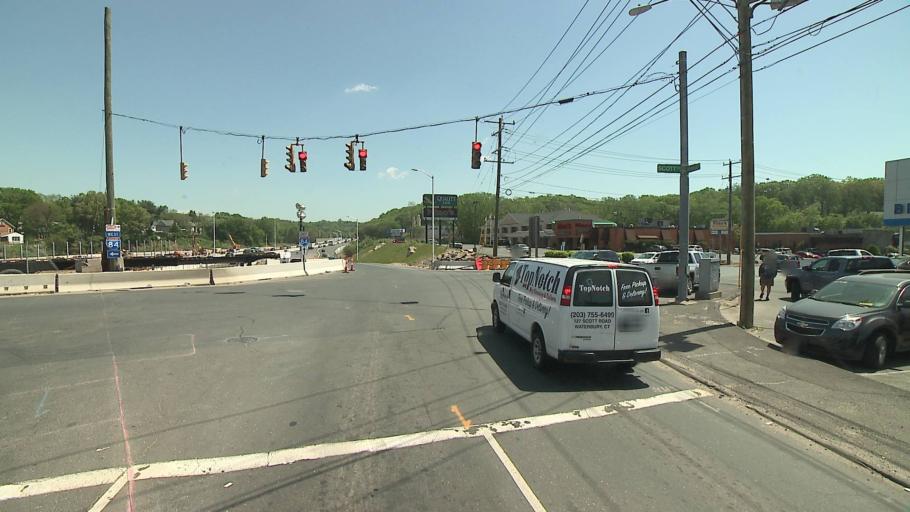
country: US
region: Connecticut
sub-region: New Haven County
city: Prospect
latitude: 41.5405
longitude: -72.9943
